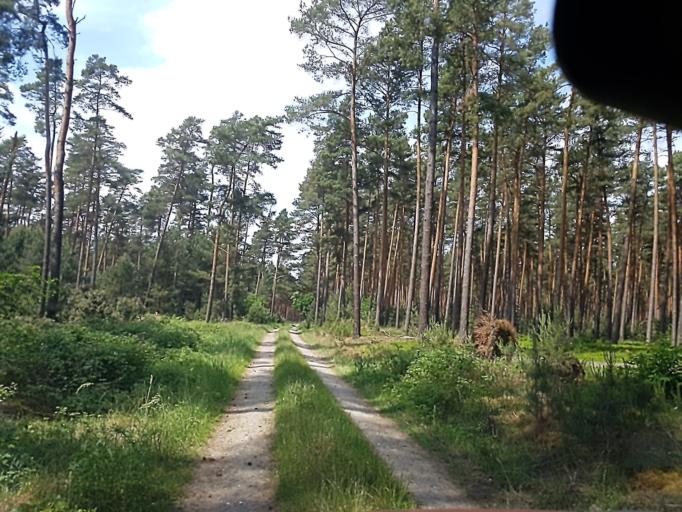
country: DE
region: Brandenburg
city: Gorzke
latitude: 52.1086
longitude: 12.3139
